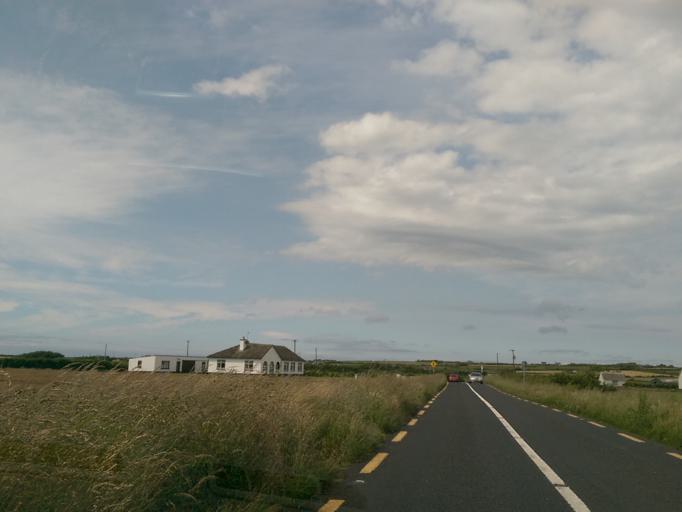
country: IE
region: Munster
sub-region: An Clar
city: Kilrush
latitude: 52.7796
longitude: -9.4417
